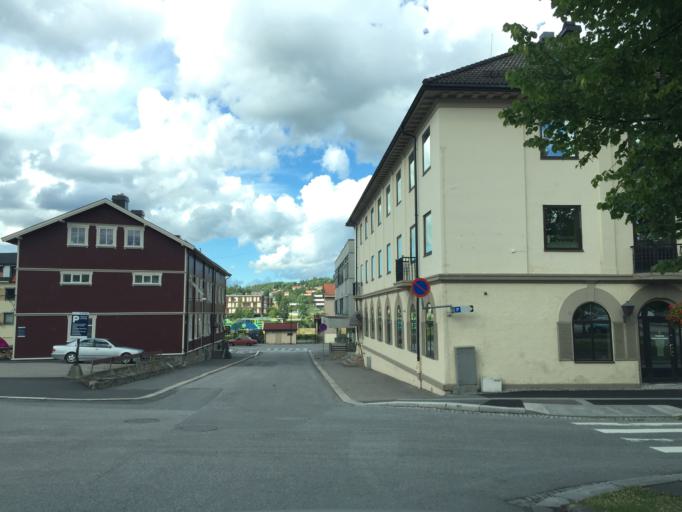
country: NO
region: Hedmark
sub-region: Kongsvinger
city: Kongsvinger
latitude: 60.1866
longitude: 12.0013
